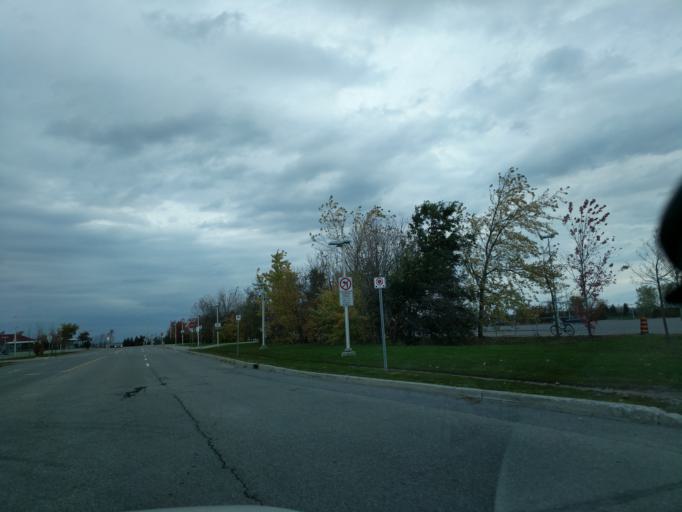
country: CA
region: Ontario
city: Bells Corners
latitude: 45.2977
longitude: -75.7347
